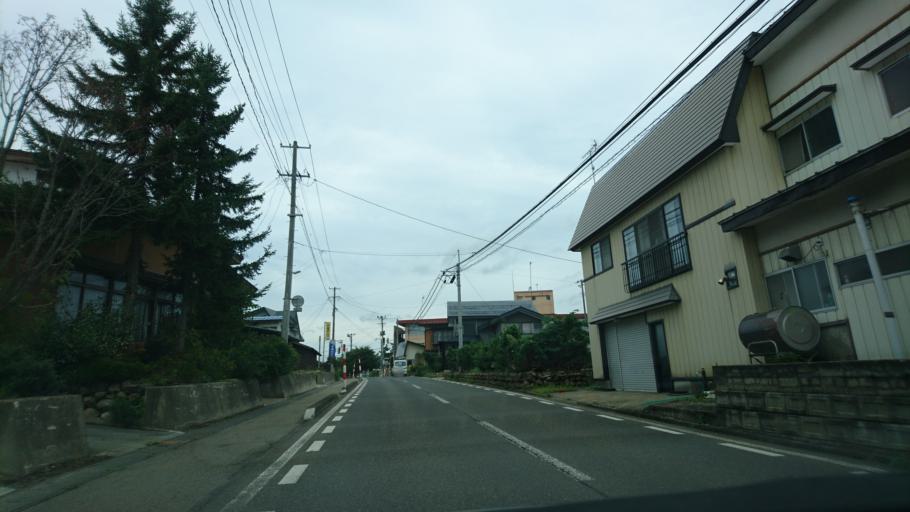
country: JP
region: Akita
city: Yuzawa
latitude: 39.1750
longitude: 140.5560
